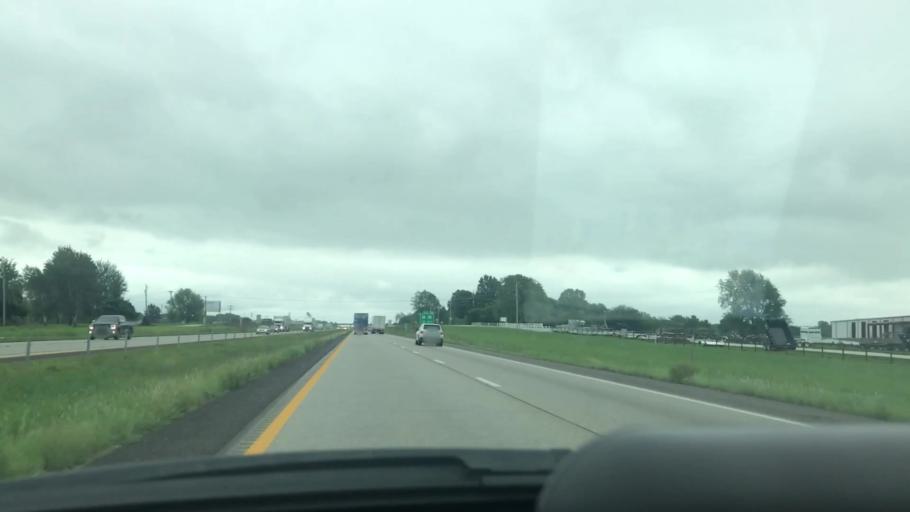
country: US
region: Missouri
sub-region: Greene County
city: Republic
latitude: 37.1978
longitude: -93.4357
